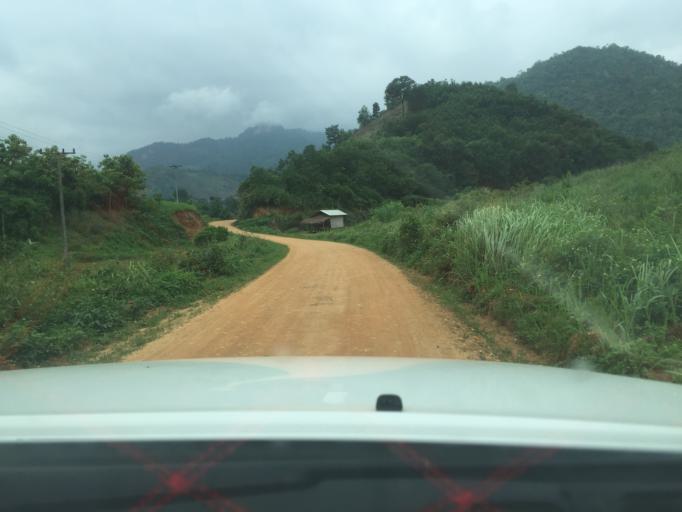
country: TH
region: Phayao
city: Phu Sang
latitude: 19.7324
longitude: 100.4796
